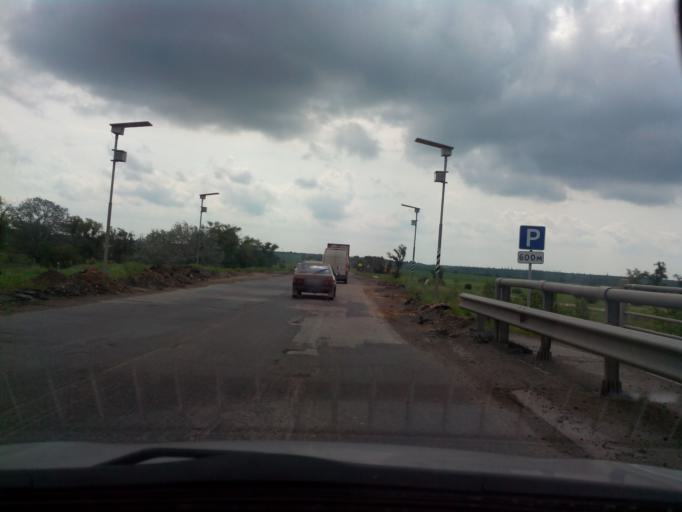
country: RU
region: Volgograd
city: Mikhaylovka
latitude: 49.9998
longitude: 43.2358
